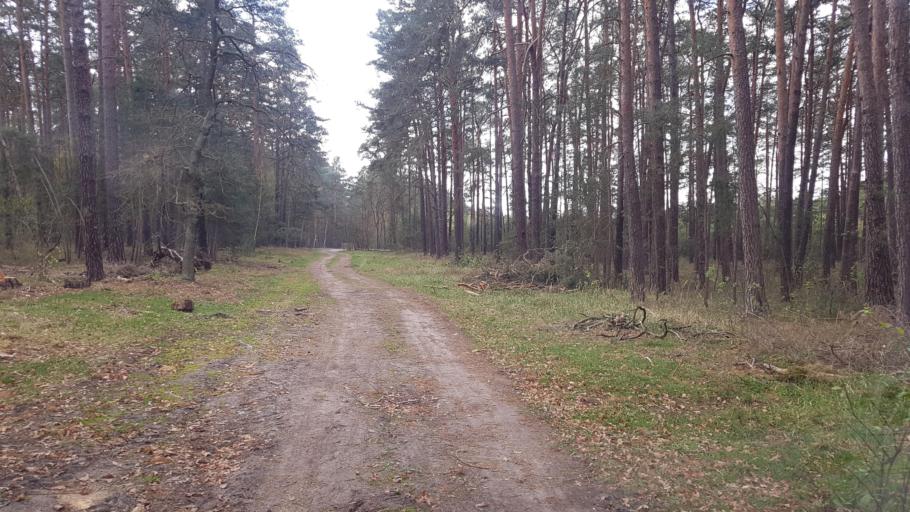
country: DE
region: Brandenburg
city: Luckenwalde
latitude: 52.1392
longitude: 13.1897
